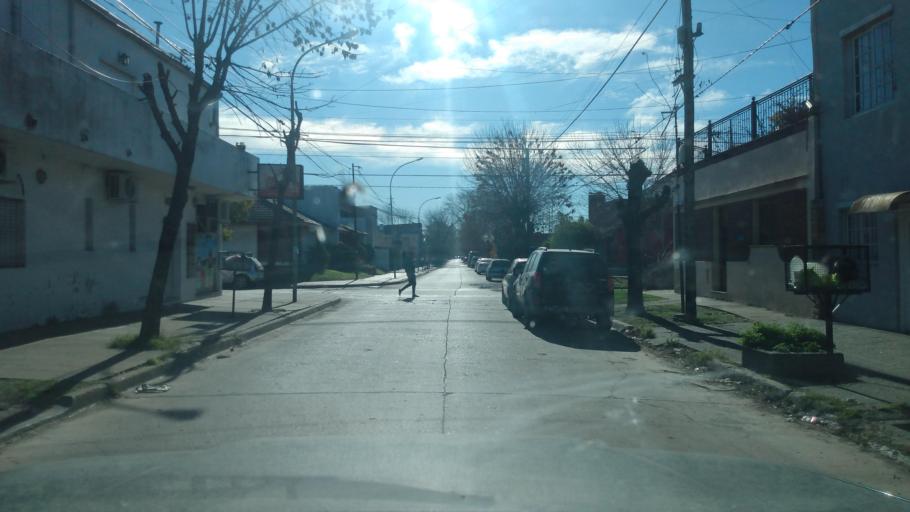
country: AR
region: Buenos Aires
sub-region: Partido de Lujan
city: Lujan
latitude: -34.5688
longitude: -59.1021
